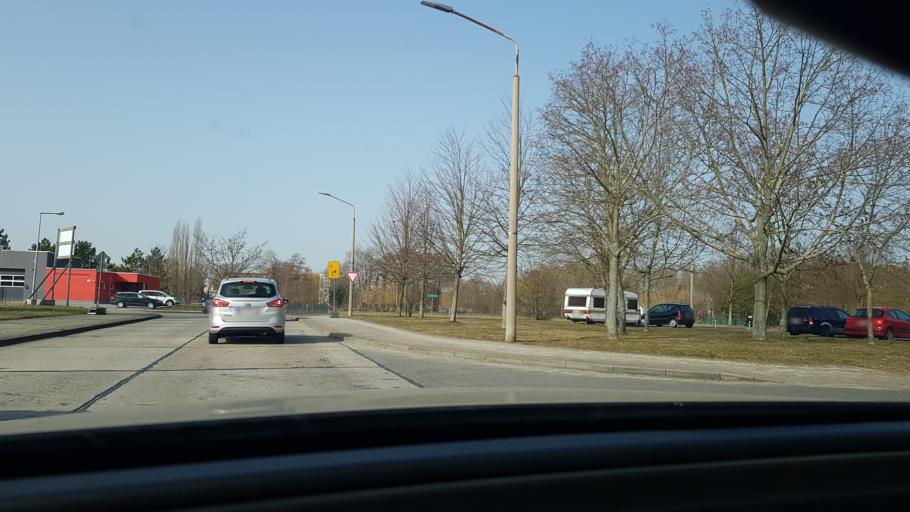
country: DE
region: Brandenburg
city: Peitz
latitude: 51.8564
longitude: 14.4198
